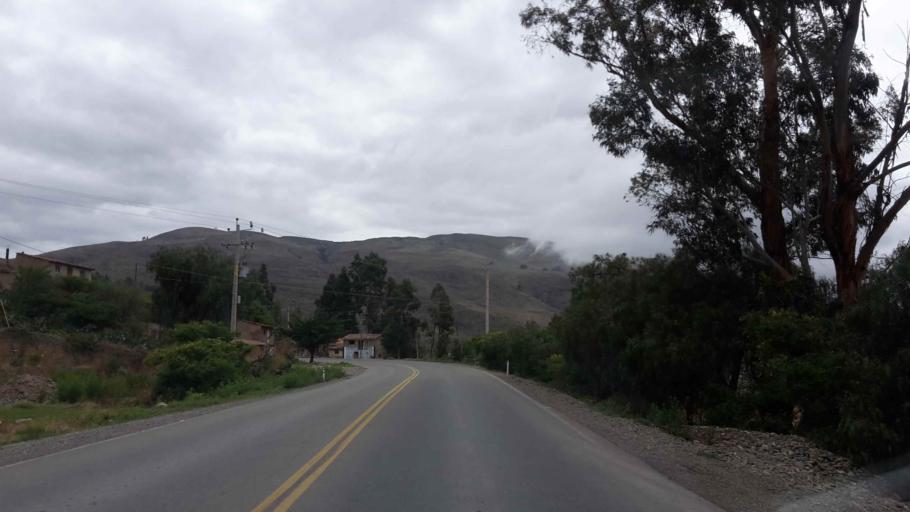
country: BO
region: Cochabamba
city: Punata
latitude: -17.5136
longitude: -65.8146
